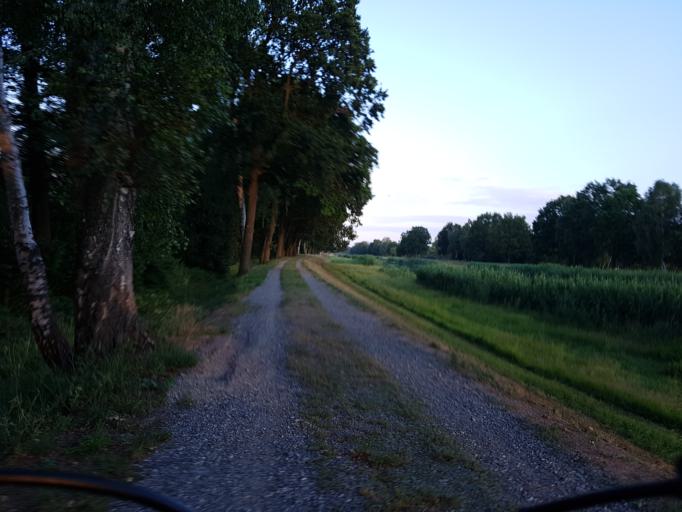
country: DE
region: Brandenburg
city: Schilda
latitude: 51.5818
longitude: 13.3407
